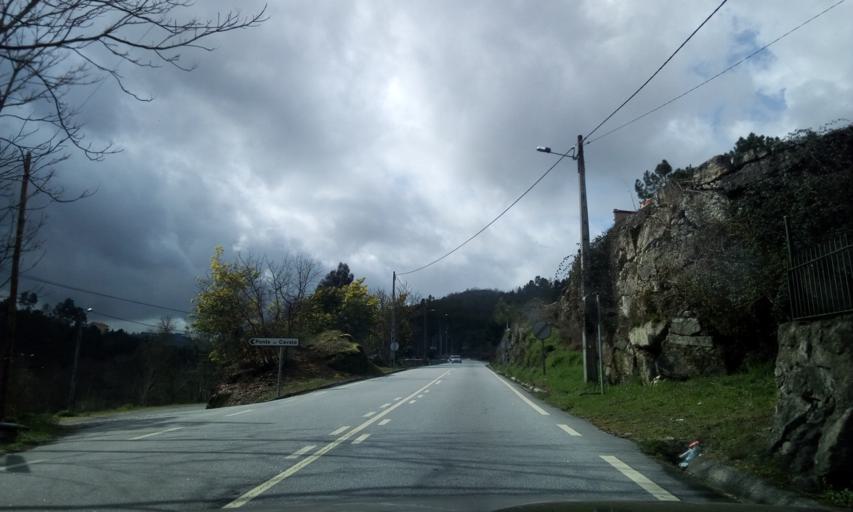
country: PT
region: Viseu
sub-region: Mangualde
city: Mangualde
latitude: 40.6431
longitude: -7.7375
